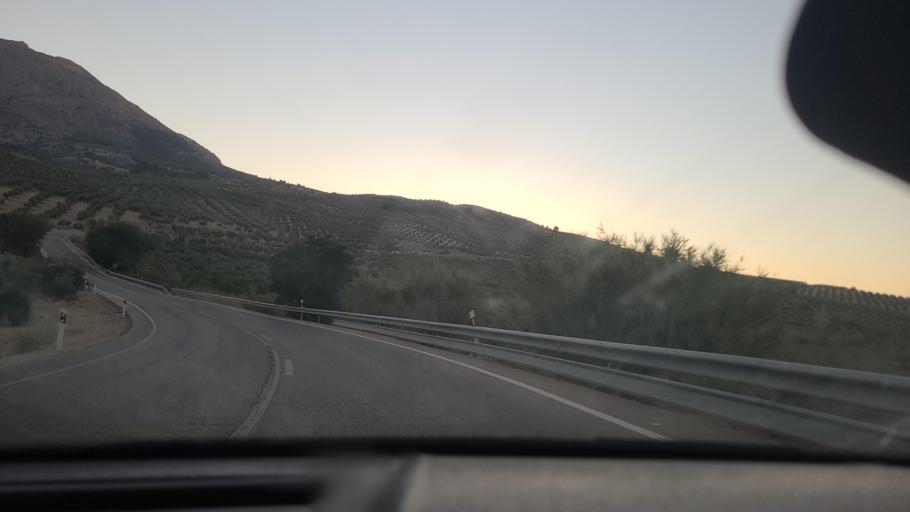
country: ES
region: Andalusia
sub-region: Provincia de Jaen
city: Jimena
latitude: 37.8270
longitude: -3.4346
